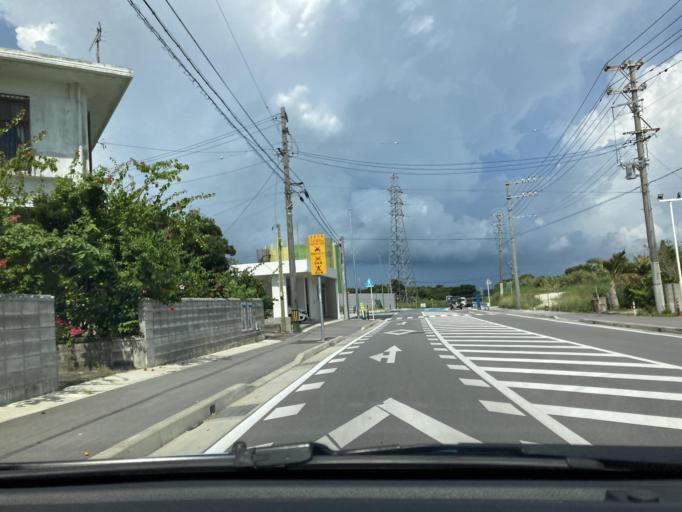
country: JP
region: Okinawa
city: Tomigusuku
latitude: 26.1622
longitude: 127.7743
